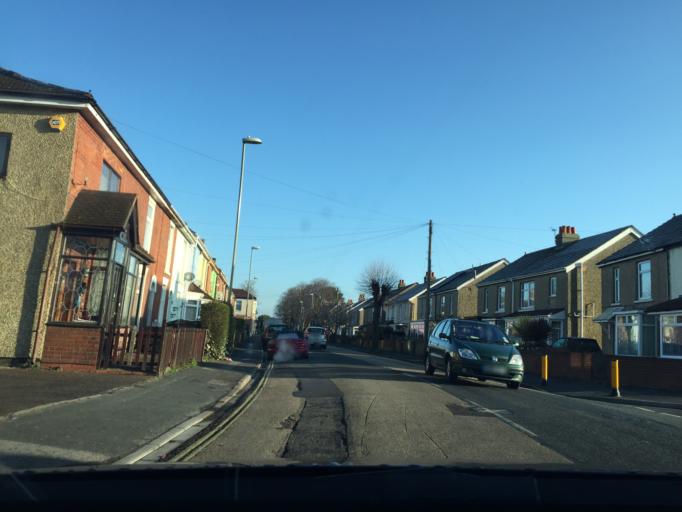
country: GB
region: England
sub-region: Hampshire
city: Gosport
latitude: 50.7955
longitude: -1.1486
